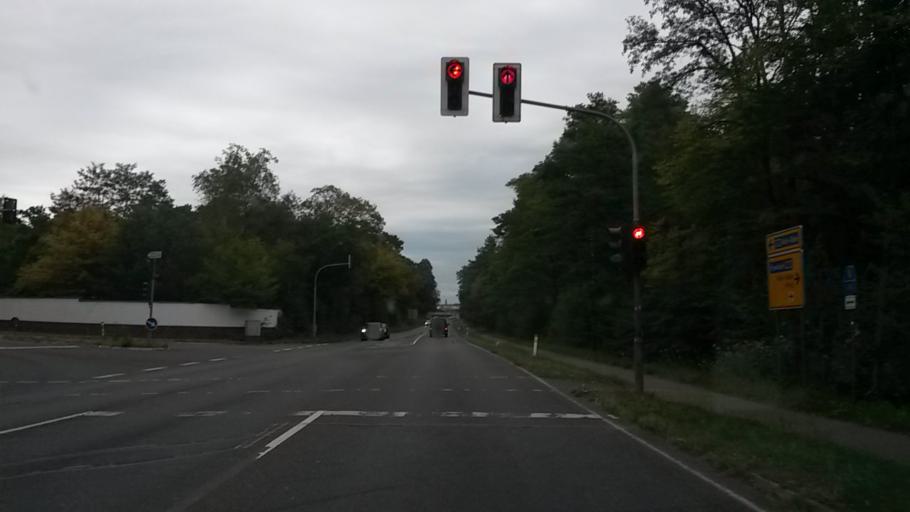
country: DE
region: North Rhine-Westphalia
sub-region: Regierungsbezirk Koln
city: Rath
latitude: 50.9445
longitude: 7.1187
